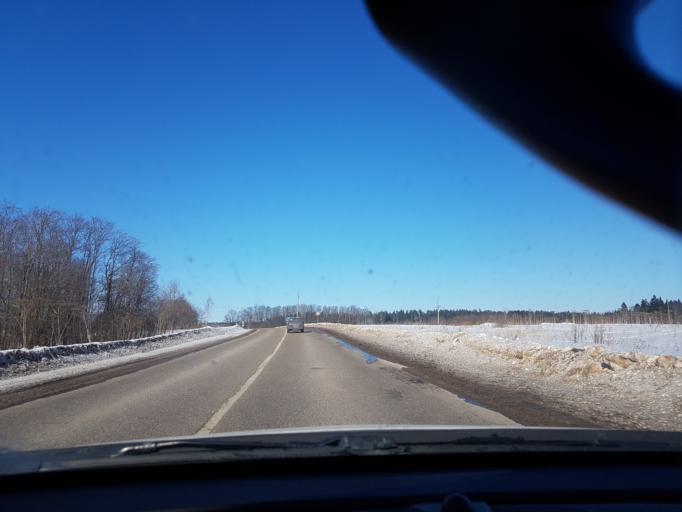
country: RU
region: Moskovskaya
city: Sychevo
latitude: 56.0035
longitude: 36.2370
